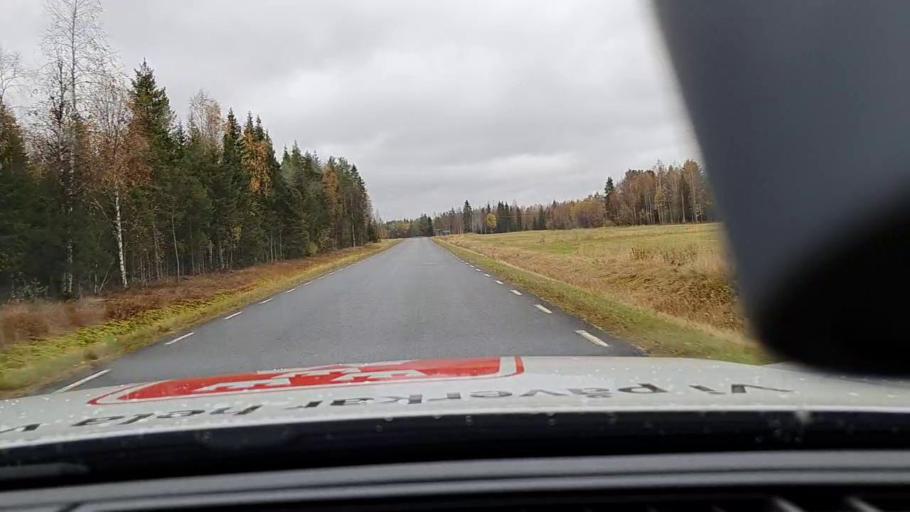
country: SE
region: Norrbotten
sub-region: Haparanda Kommun
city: Haparanda
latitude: 65.9305
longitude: 23.8166
